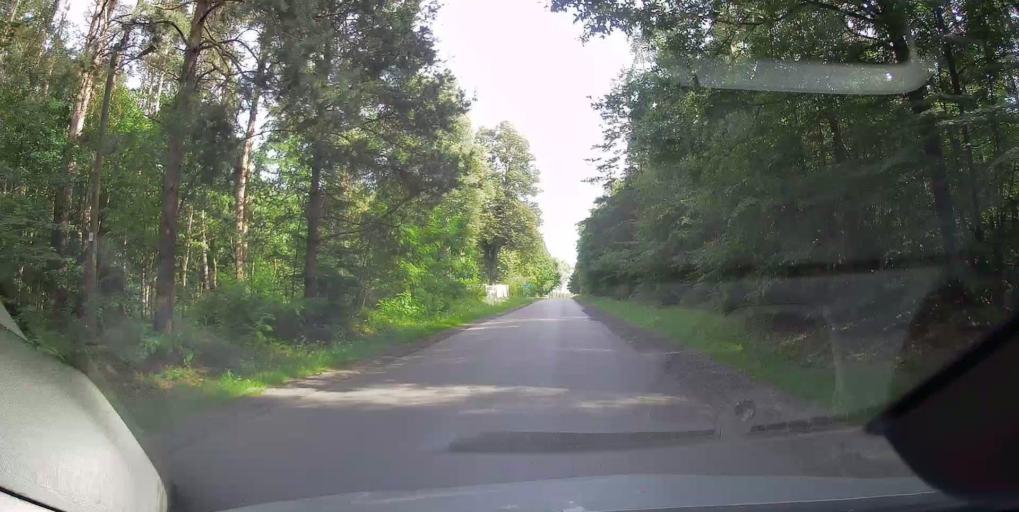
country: PL
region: Lodz Voivodeship
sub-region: Powiat tomaszowski
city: Tomaszow Mazowiecki
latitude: 51.4641
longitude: 20.0293
